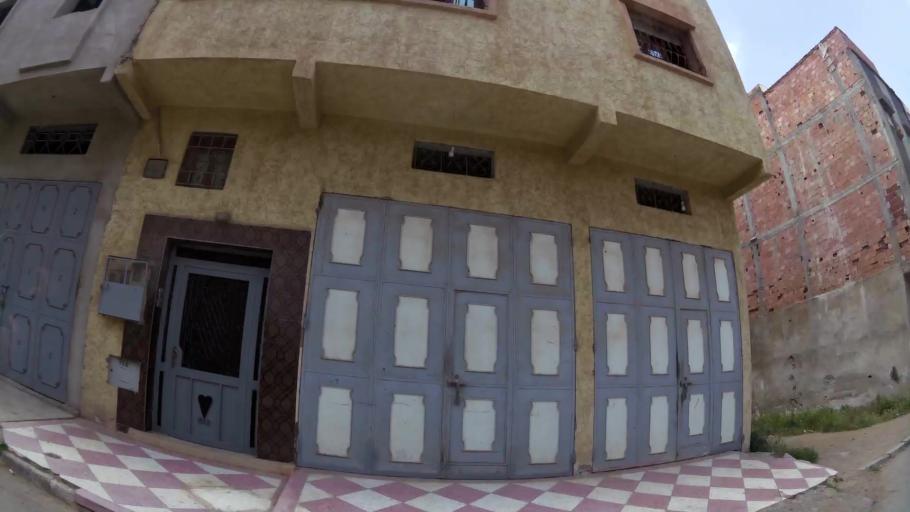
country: MA
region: Rabat-Sale-Zemmour-Zaer
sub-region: Khemisset
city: Tiflet
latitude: 34.0096
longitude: -6.5322
